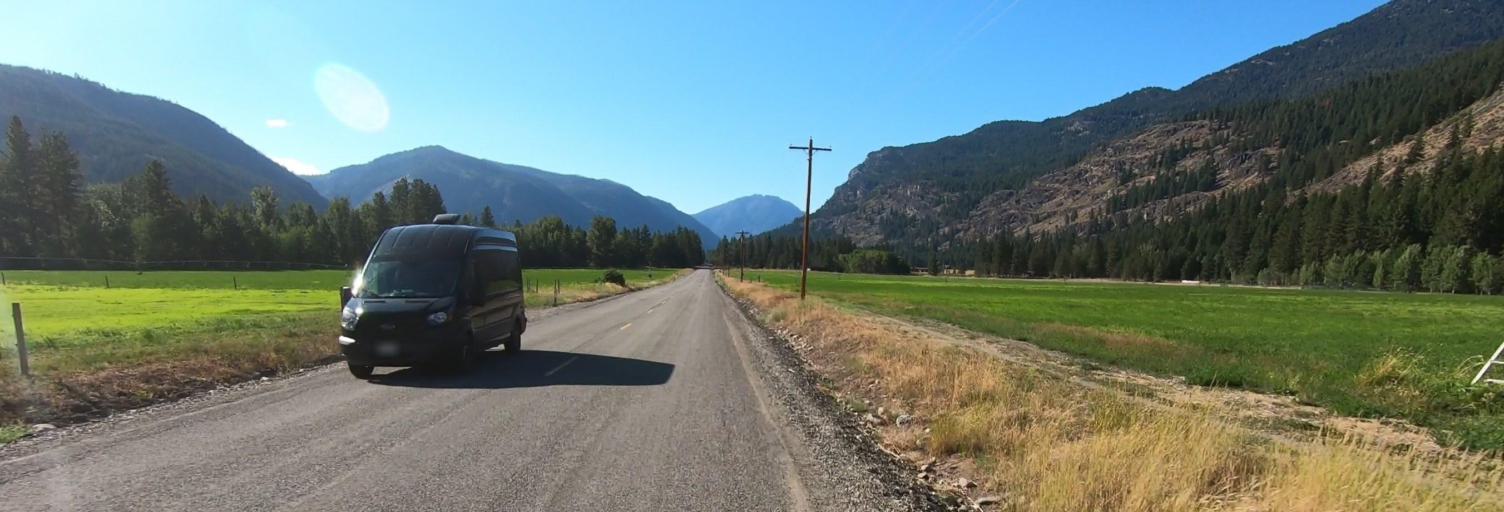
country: US
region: Washington
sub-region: Chelan County
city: Granite Falls
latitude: 48.5851
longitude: -120.3883
